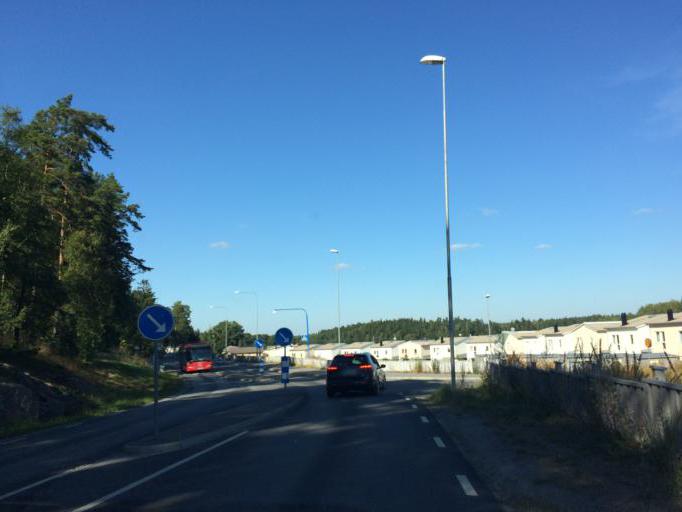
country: SE
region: Stockholm
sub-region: Upplands Vasby Kommun
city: Upplands Vaesby
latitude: 59.5051
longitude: 17.9511
